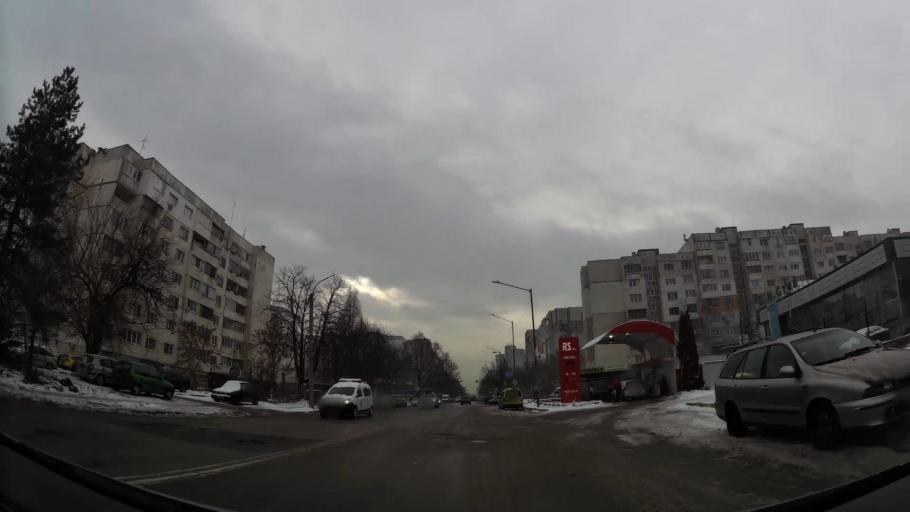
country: BG
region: Sofia-Capital
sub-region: Stolichna Obshtina
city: Sofia
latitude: 42.7148
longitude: 23.2977
